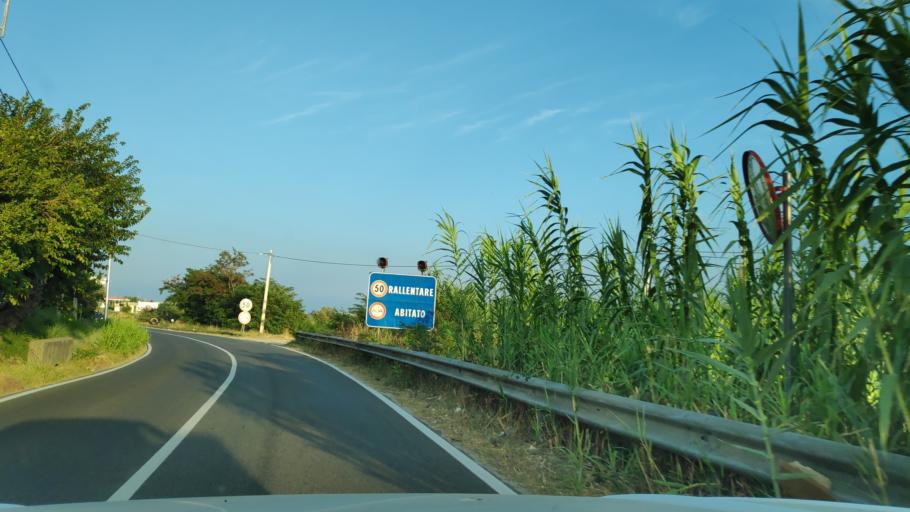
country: IT
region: Calabria
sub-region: Provincia di Catanzaro
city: Martelli-Laganosa
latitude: 38.6793
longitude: 16.5190
